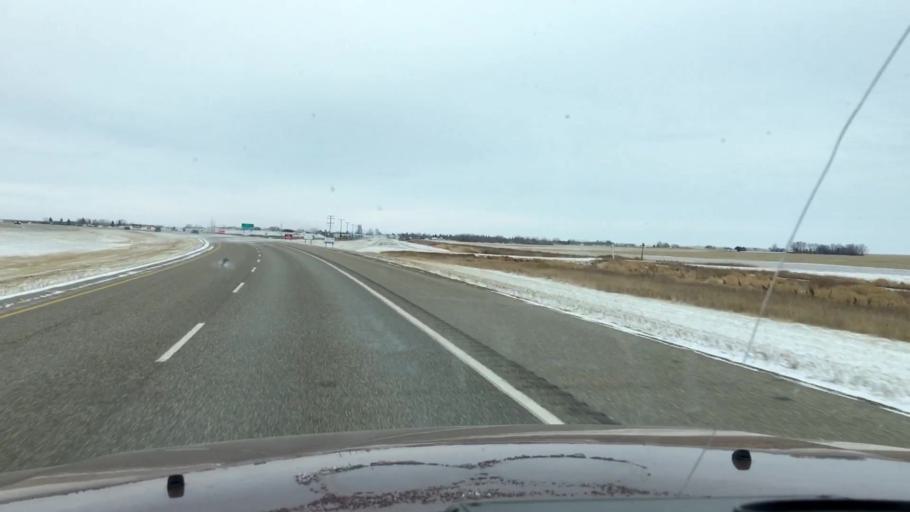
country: CA
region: Saskatchewan
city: Watrous
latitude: 51.0678
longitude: -105.8372
